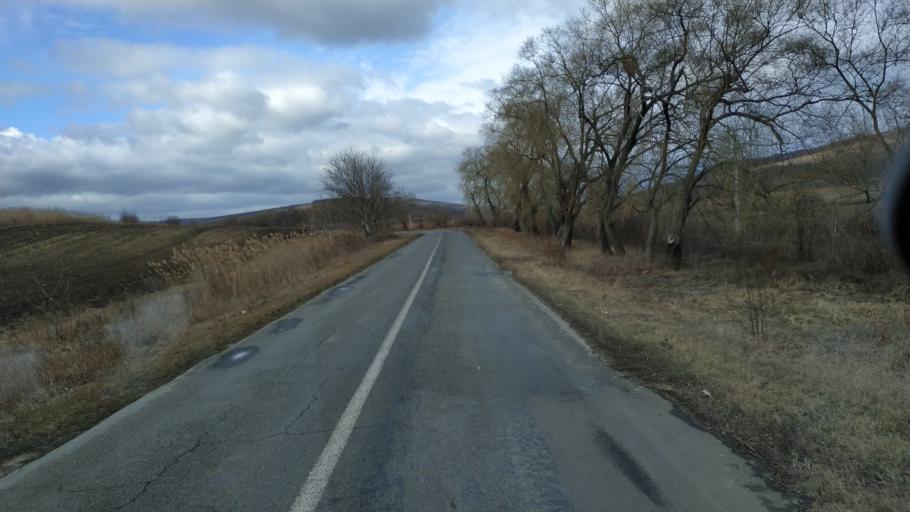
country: MD
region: Stinga Nistrului
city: Bucovat
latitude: 47.1434
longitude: 28.3642
